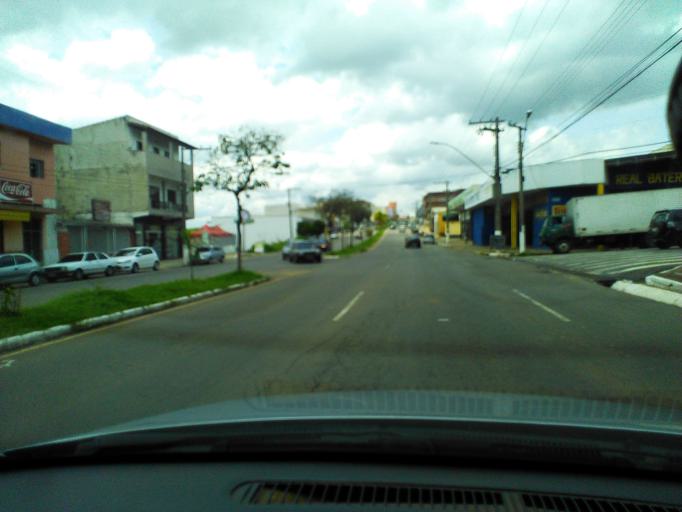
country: BR
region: Minas Gerais
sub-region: Tres Coracoes
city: Tres Coracoes
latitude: -21.6847
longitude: -45.2637
